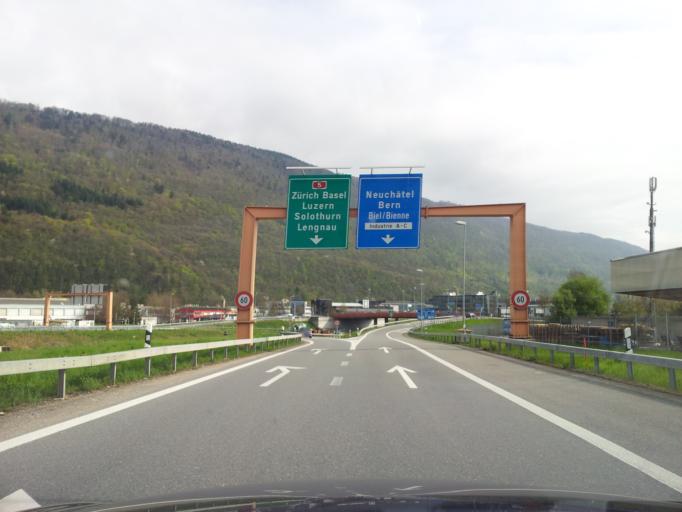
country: CH
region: Bern
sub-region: Biel/Bienne District
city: Orpund
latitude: 47.1574
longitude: 7.2852
